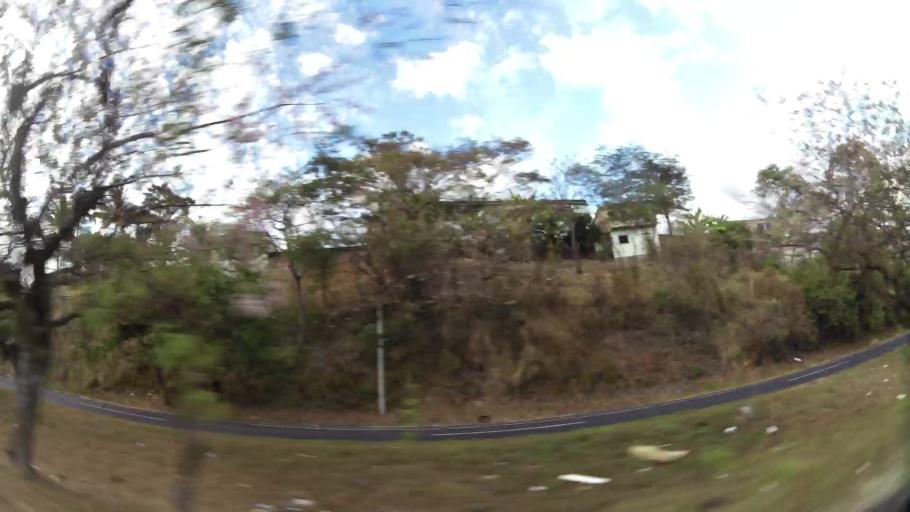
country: SV
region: Cuscatlan
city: Cojutepeque
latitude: 13.7288
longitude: -88.8845
